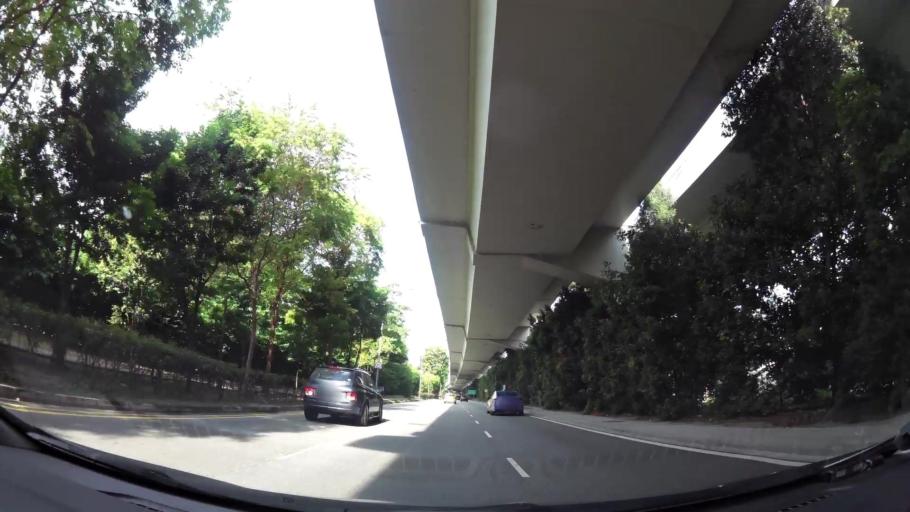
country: SG
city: Singapore
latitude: 1.2765
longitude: 103.7910
